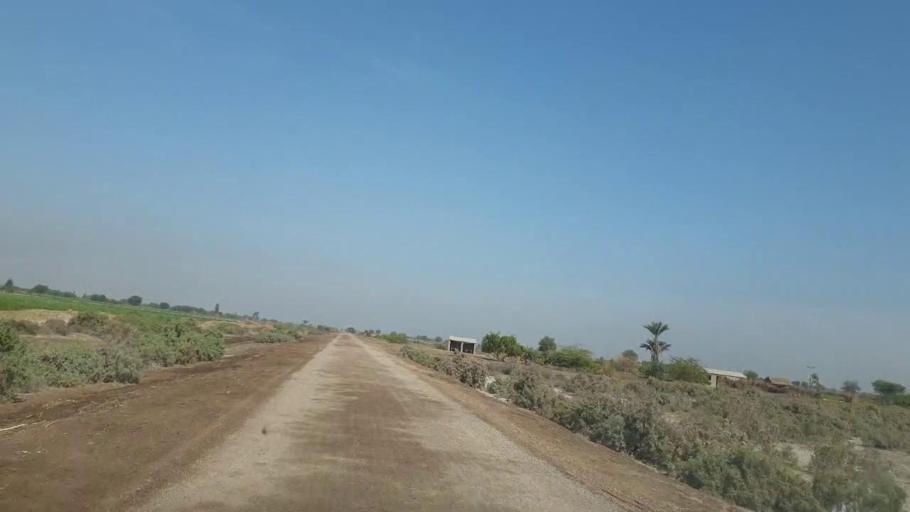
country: PK
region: Sindh
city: Mirpur Khas
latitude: 25.5721
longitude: 69.1845
